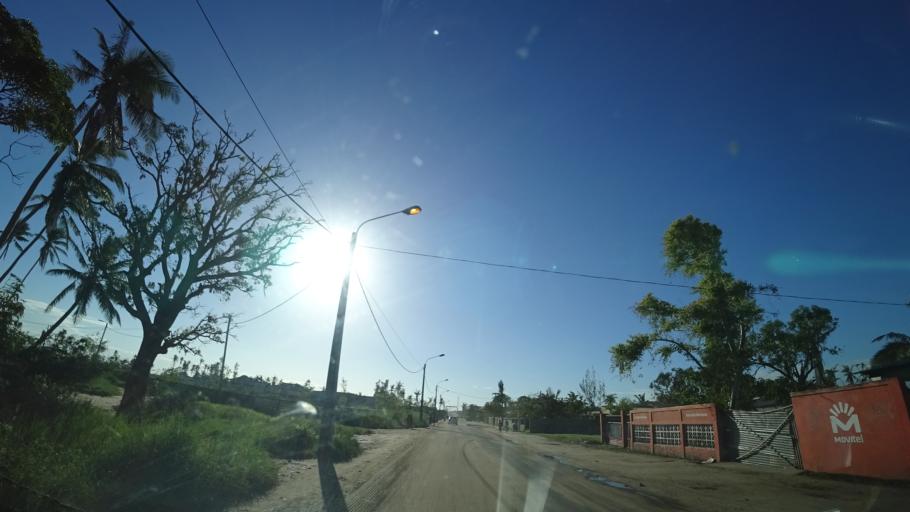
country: MZ
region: Sofala
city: Beira
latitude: -19.7872
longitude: 34.8833
